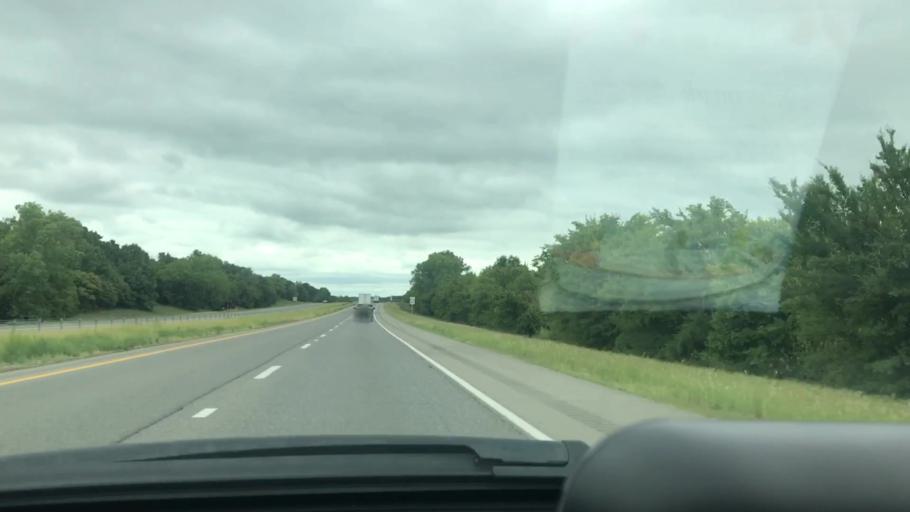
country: US
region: Oklahoma
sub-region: McIntosh County
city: Eufaula
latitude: 35.3678
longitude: -95.5724
